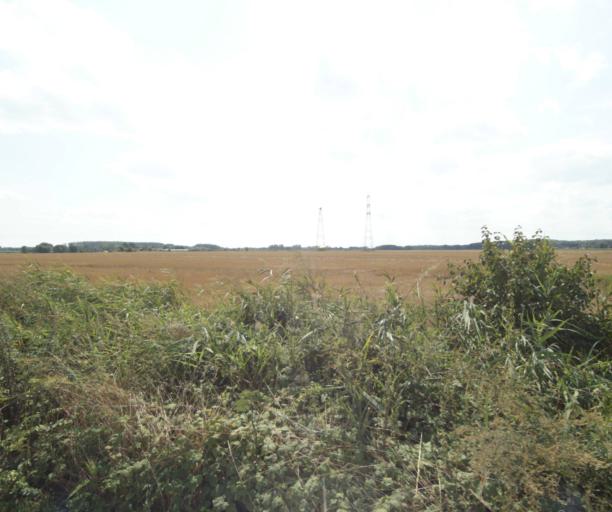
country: FR
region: Nord-Pas-de-Calais
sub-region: Departement du Nord
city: Hem
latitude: 50.6463
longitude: 3.1810
